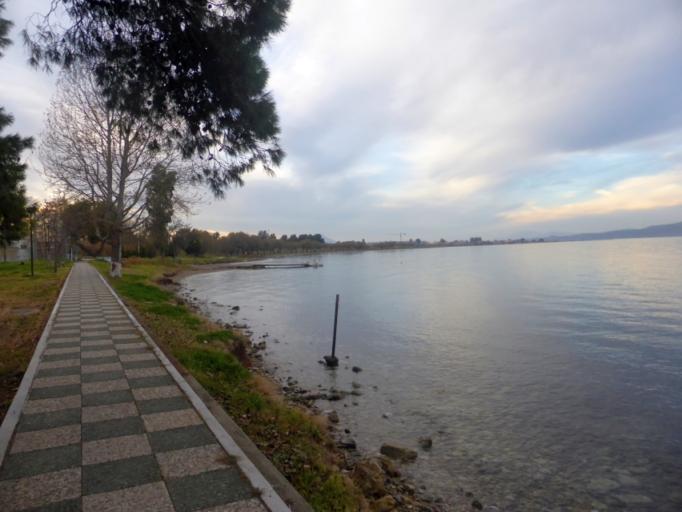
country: GR
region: Attica
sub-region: Nomarchia Anatolikis Attikis
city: Skala Oropou
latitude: 38.3225
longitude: 23.7855
